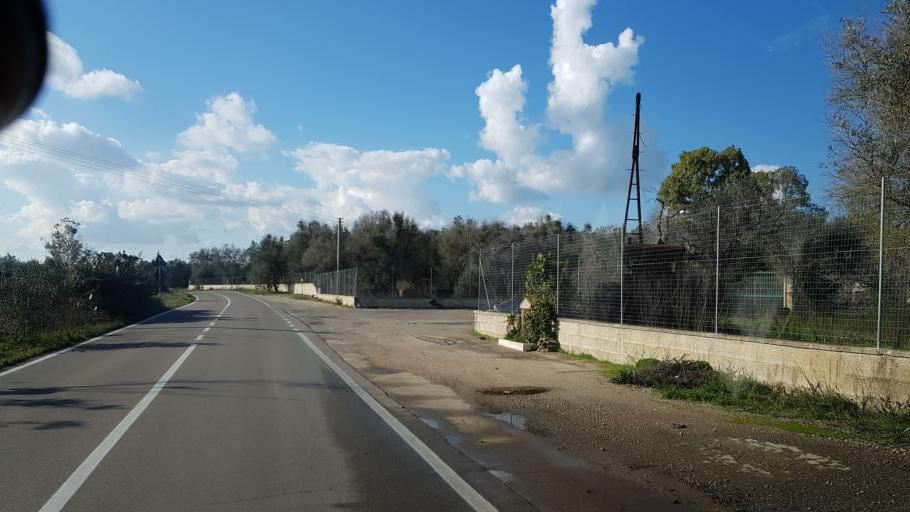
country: IT
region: Apulia
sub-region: Provincia di Lecce
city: Trepuzzi
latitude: 40.4424
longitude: 18.0915
